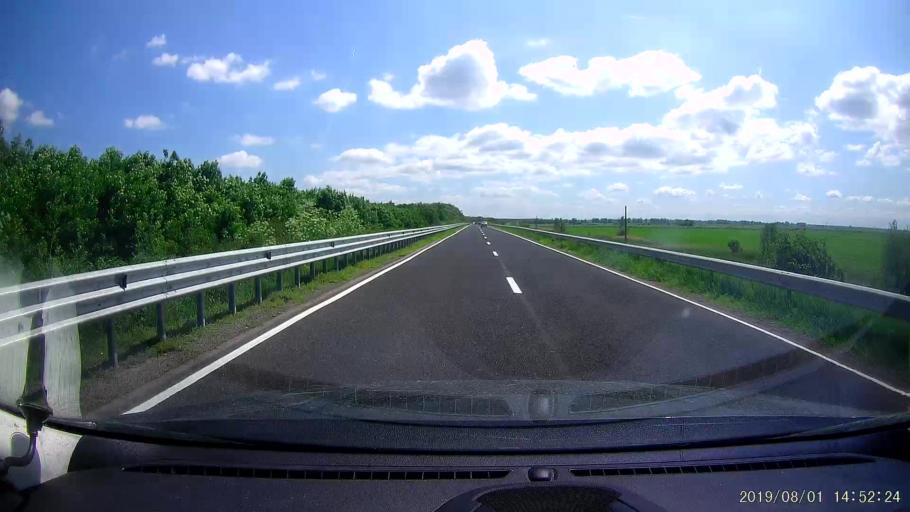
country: RO
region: Braila
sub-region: Comuna Vadeni
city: Vadeni
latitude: 45.3559
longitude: 28.0111
